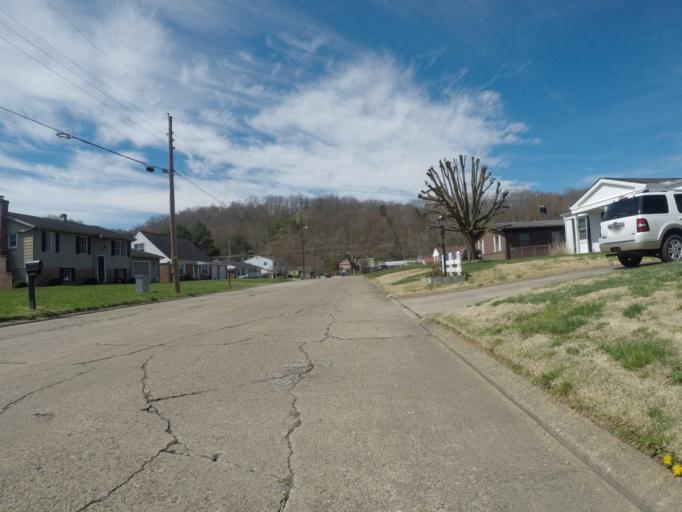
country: US
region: West Virginia
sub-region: Cabell County
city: Pea Ridge
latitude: 38.4034
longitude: -82.3179
